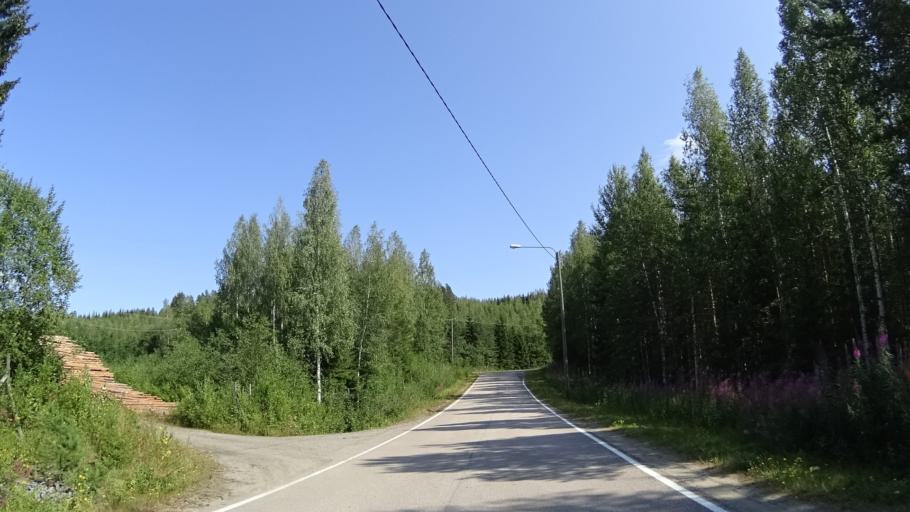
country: FI
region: Central Finland
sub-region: Jaemsae
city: Jaemsae
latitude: 61.7750
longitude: 24.8910
